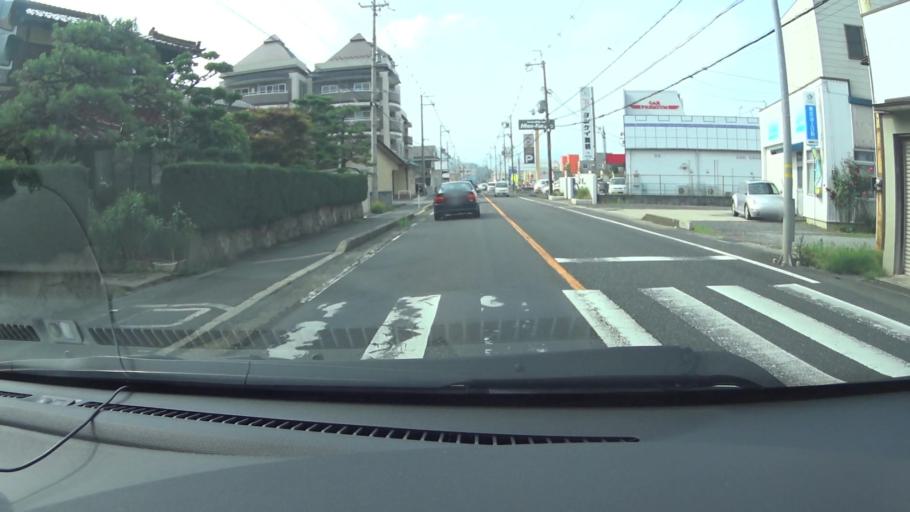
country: JP
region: Kyoto
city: Maizuru
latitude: 35.4553
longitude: 135.3497
